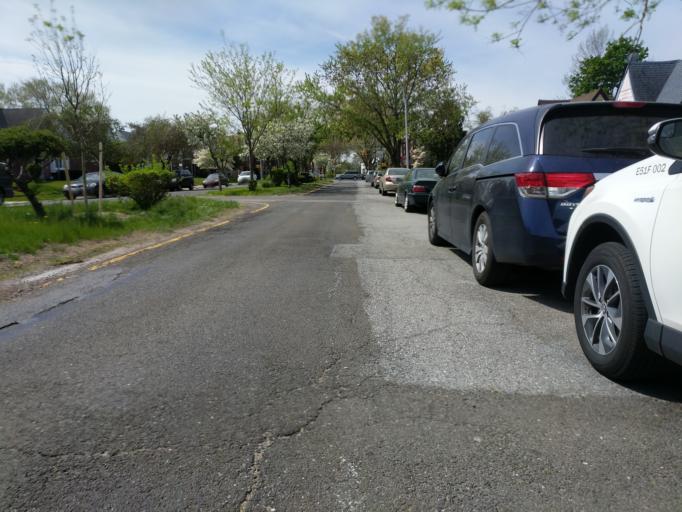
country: US
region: New York
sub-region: Nassau County
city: South Valley Stream
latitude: 40.6779
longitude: -73.7385
